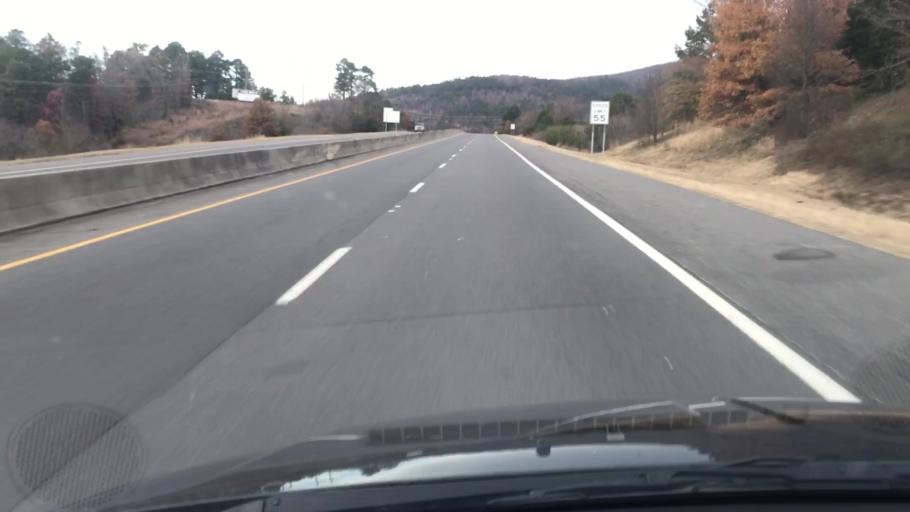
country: US
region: Arkansas
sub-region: Garland County
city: Piney
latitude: 34.4857
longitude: -93.1120
